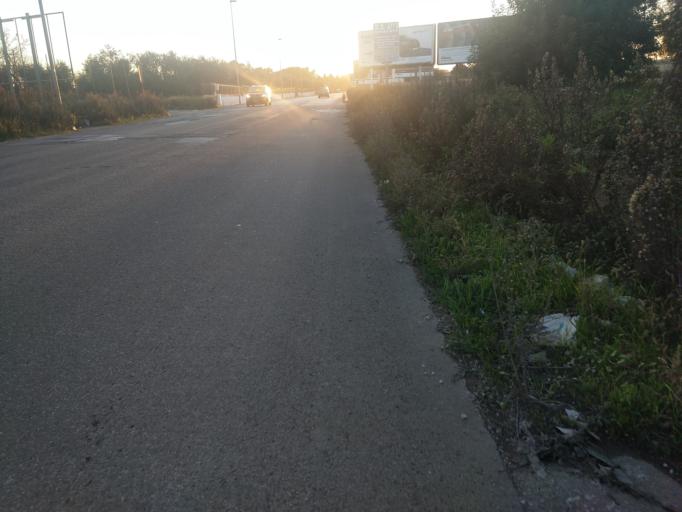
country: IT
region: Apulia
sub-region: Provincia di Bari
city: Modugno
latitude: 41.0848
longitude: 16.8005
